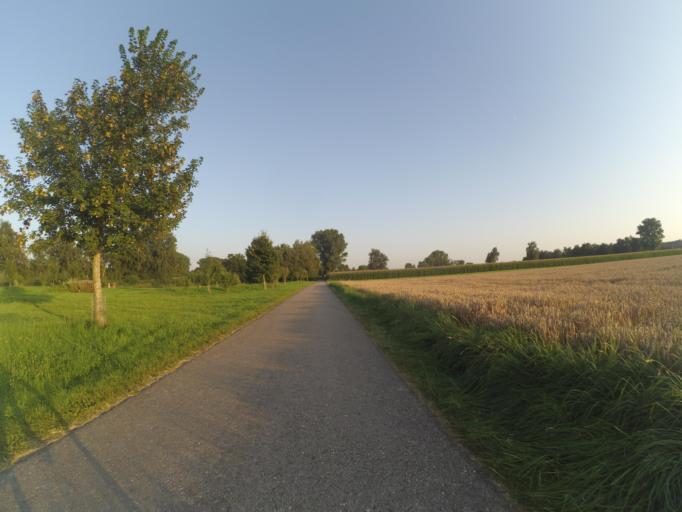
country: DE
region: Bavaria
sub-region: Swabia
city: Jengen
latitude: 47.9893
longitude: 10.7306
